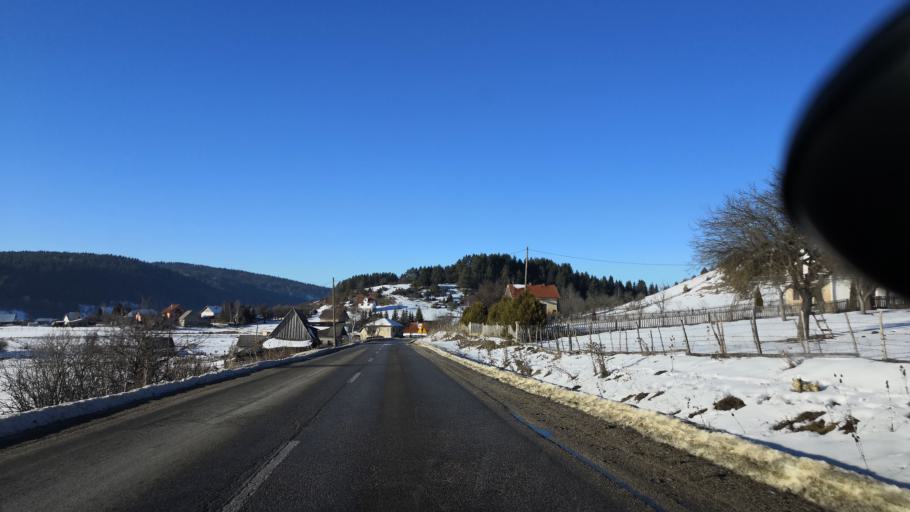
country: BA
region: Republika Srpska
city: Sokolac
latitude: 43.9995
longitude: 18.8821
